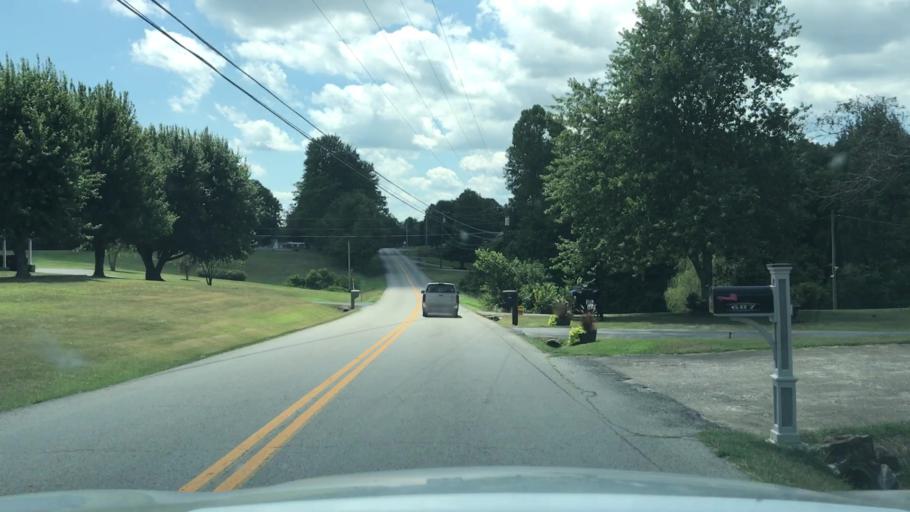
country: US
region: Kentucky
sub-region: Muhlenberg County
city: Greenville
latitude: 37.1934
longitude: -87.2153
